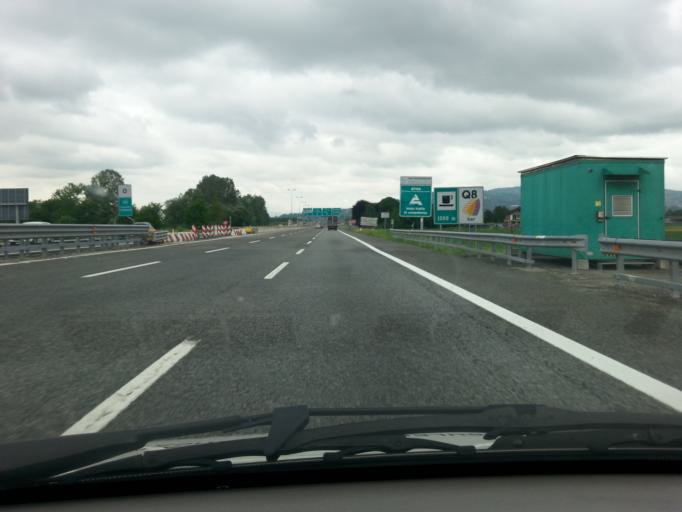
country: IT
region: Piedmont
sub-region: Provincia di Torino
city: La Loggia
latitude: 44.9638
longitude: 7.7045
